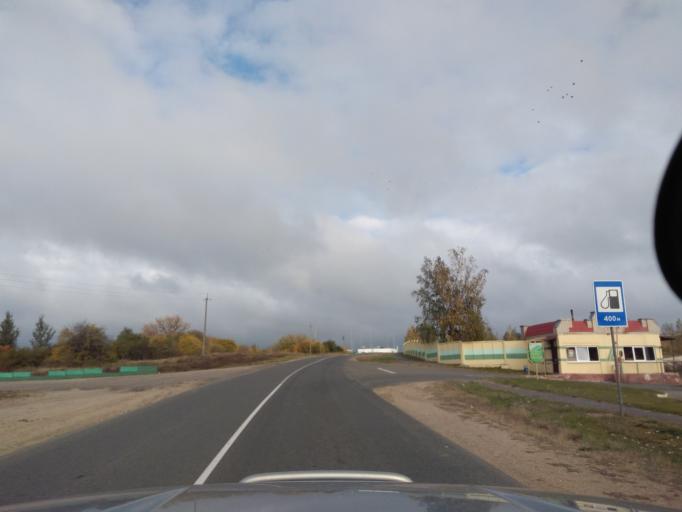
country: BY
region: Minsk
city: Kapyl'
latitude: 53.1463
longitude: 27.0760
